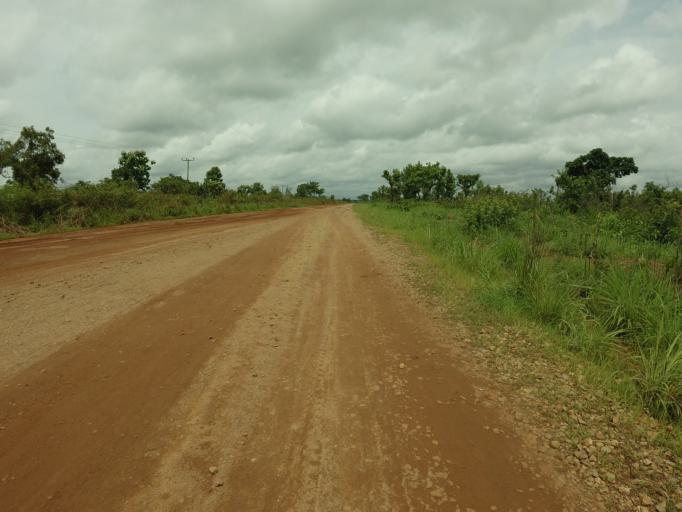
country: GH
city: Kpandae
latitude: 8.4499
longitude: 0.3496
